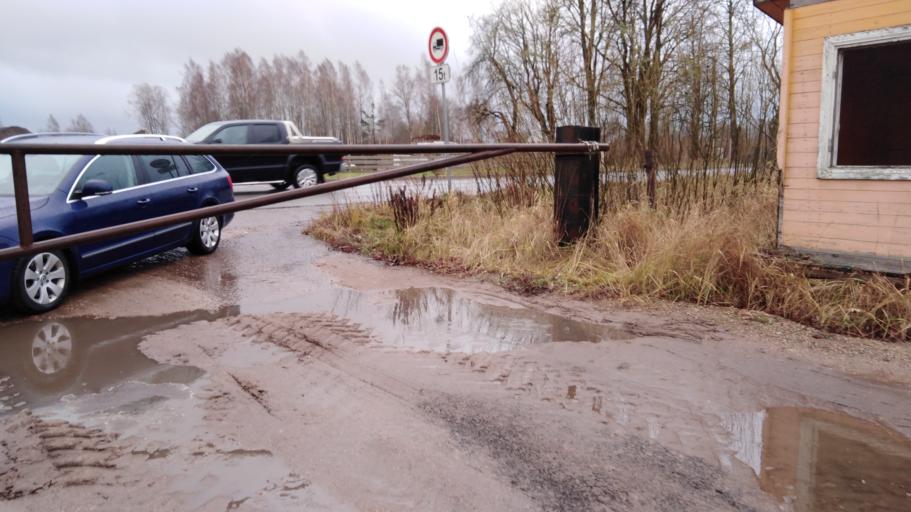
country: LV
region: Kuldigas Rajons
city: Kuldiga
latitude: 56.9618
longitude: 21.9778
